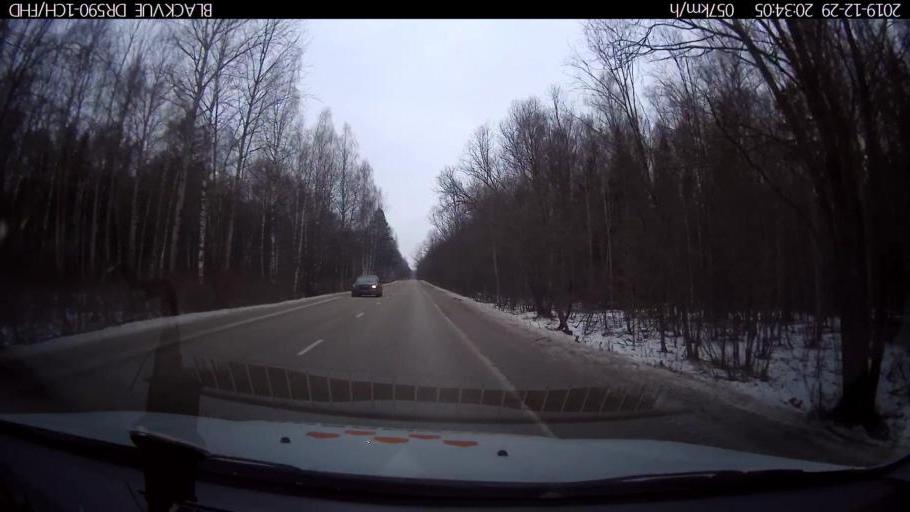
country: RU
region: Nizjnij Novgorod
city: Afonino
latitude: 56.1841
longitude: 44.0439
